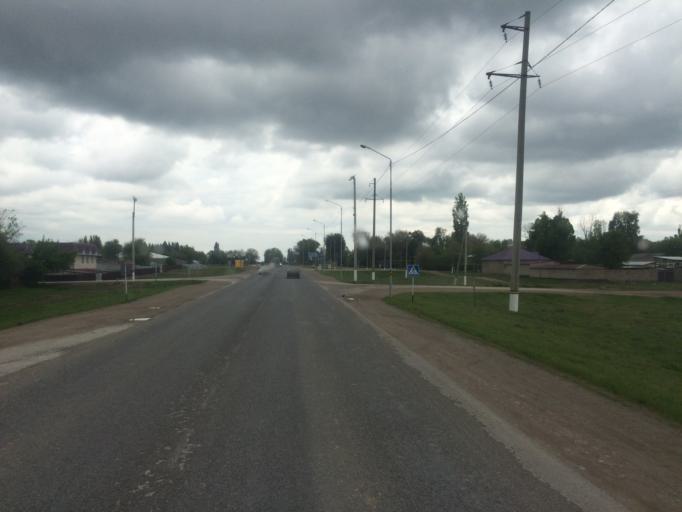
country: KZ
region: Zhambyl
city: Georgiyevka
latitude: 43.1438
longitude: 74.6152
